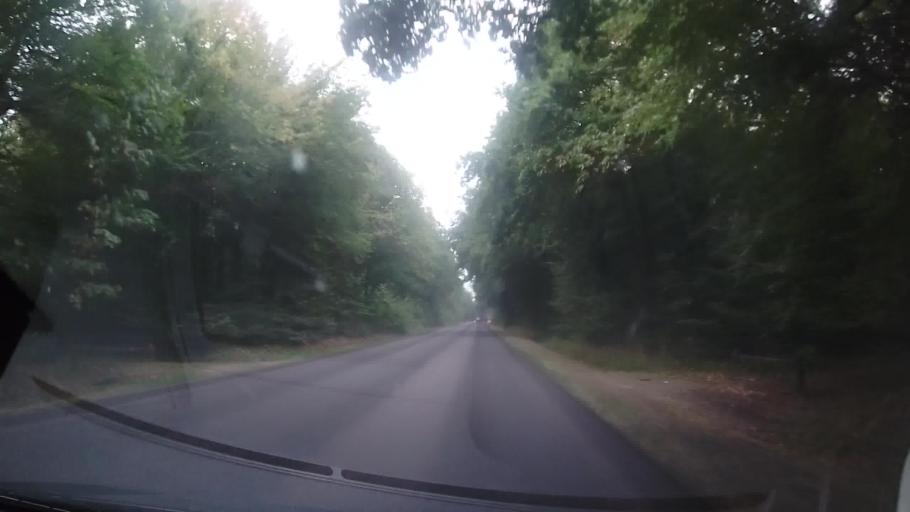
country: FR
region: Ile-de-France
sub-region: Departement de l'Essonne
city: Dourdan
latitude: 48.5463
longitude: 1.9863
